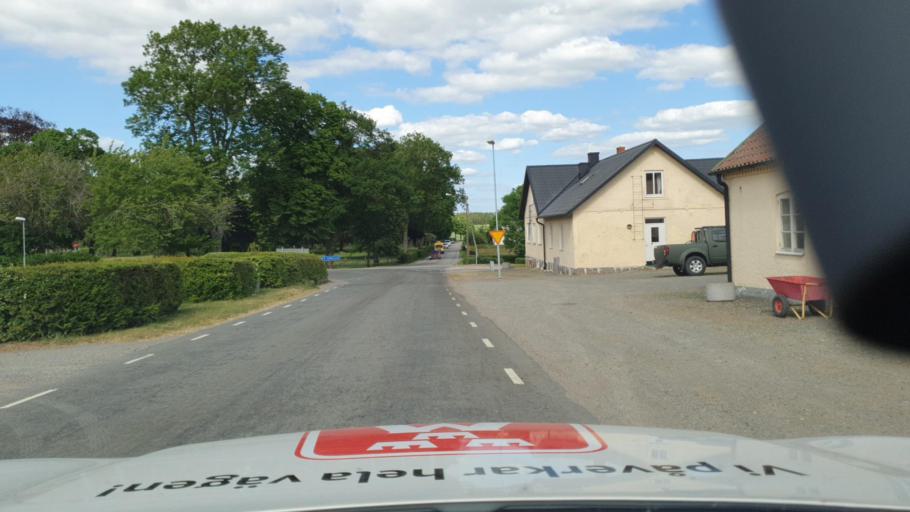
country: SE
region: Skane
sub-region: Tomelilla Kommun
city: Tomelilla
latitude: 55.4893
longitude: 14.0457
